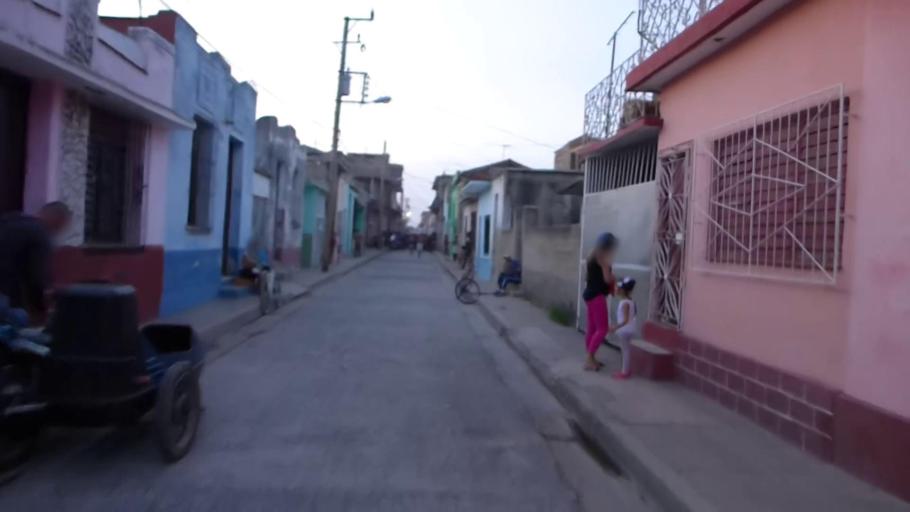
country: CU
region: Camaguey
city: Camaguey
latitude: 21.3748
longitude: -77.9198
